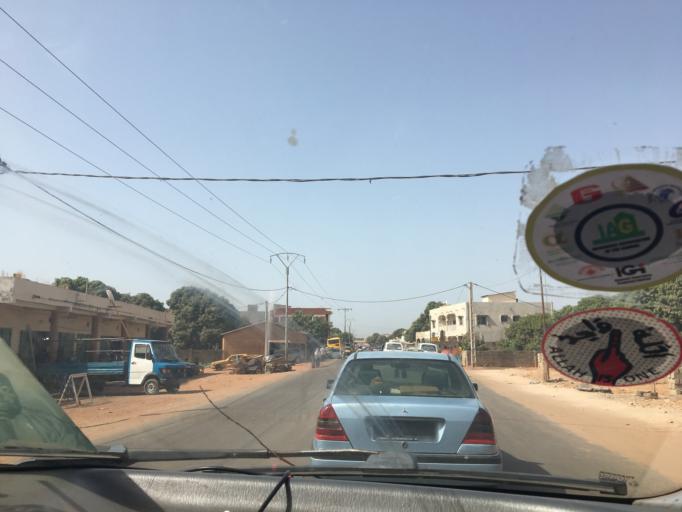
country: GM
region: Western
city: Abuko
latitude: 13.3862
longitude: -16.6772
